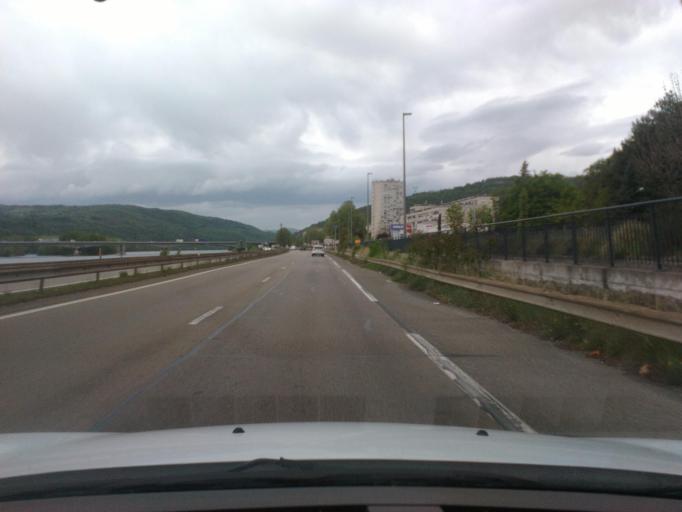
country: FR
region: Rhone-Alpes
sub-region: Departement du Rhone
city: Saint-Romain-en-Gal
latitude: 45.5385
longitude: 4.8647
